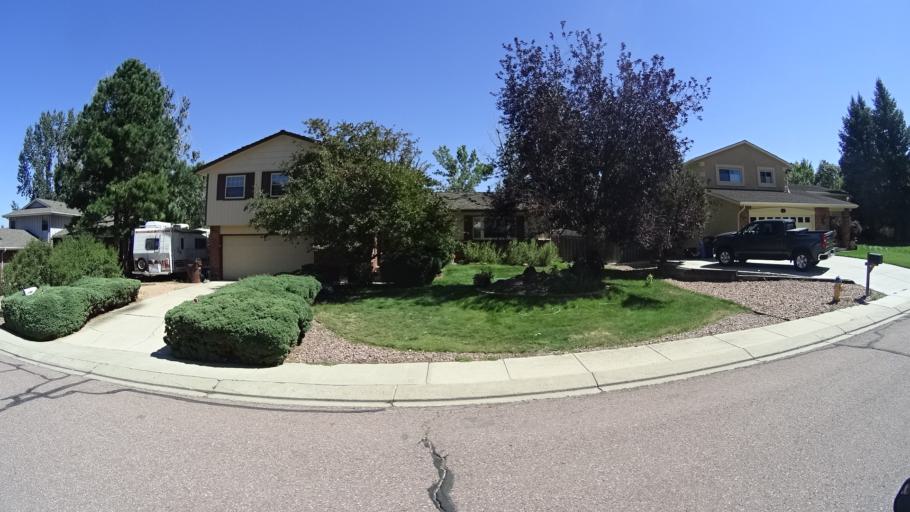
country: US
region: Colorado
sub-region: El Paso County
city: Air Force Academy
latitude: 38.9250
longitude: -104.8057
